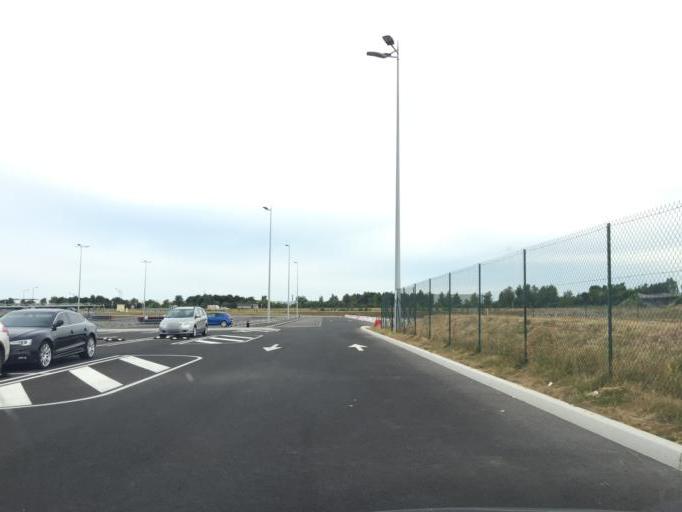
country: FR
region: Auvergne
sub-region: Departement de l'Allier
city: Moulins
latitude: 46.5889
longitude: 3.3319
